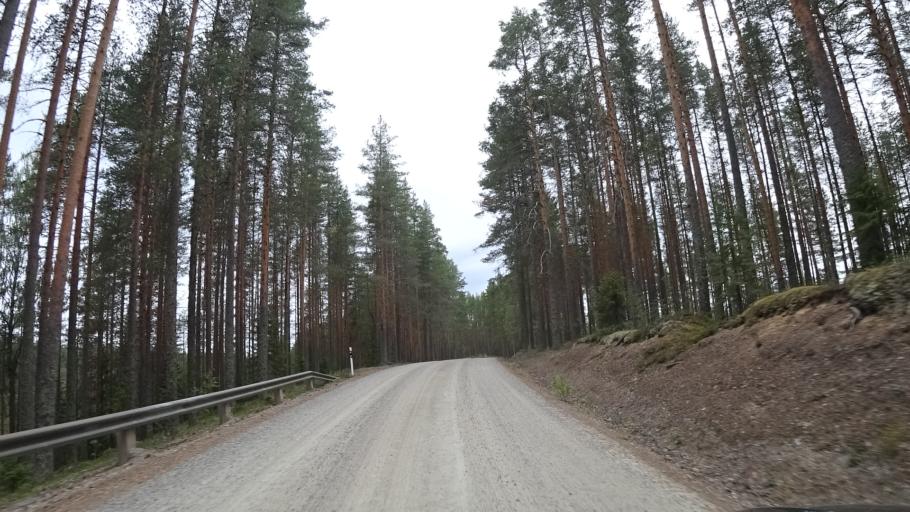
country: FI
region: North Karelia
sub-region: Pielisen Karjala
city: Lieksa
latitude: 63.2443
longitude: 30.3424
